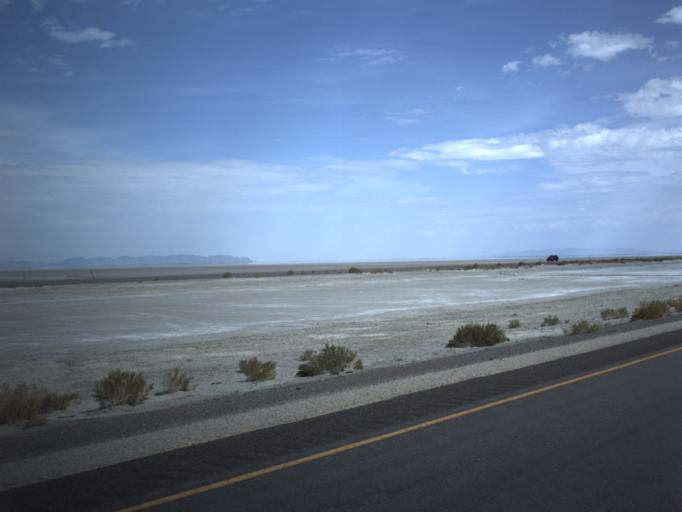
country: US
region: Utah
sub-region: Tooele County
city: Wendover
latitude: 40.7365
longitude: -113.7535
